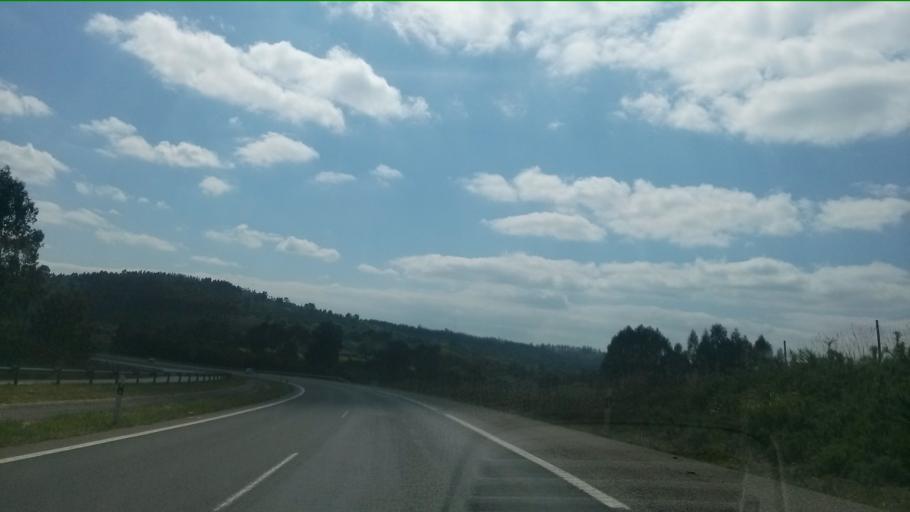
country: ES
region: Galicia
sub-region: Provincia da Coruna
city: Oroso
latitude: 42.9113
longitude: -8.4583
